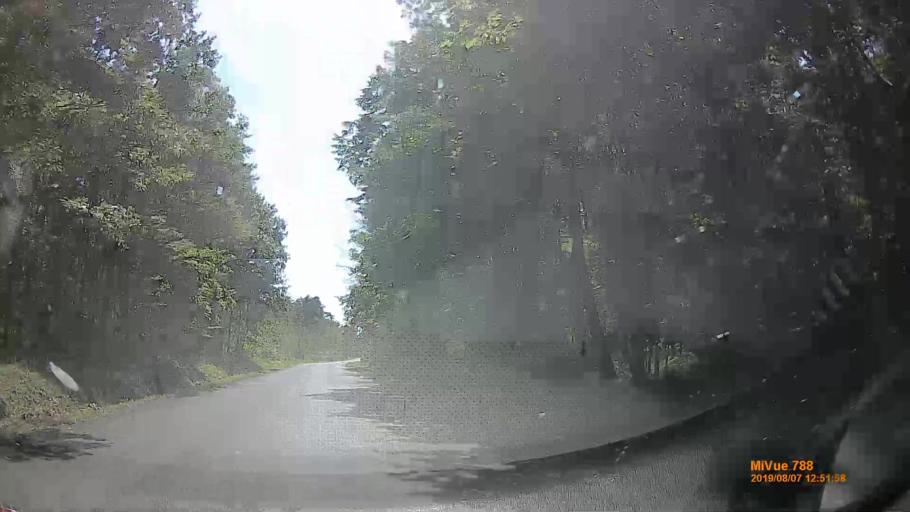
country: HU
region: Zala
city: Cserszegtomaj
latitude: 46.8538
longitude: 17.2670
